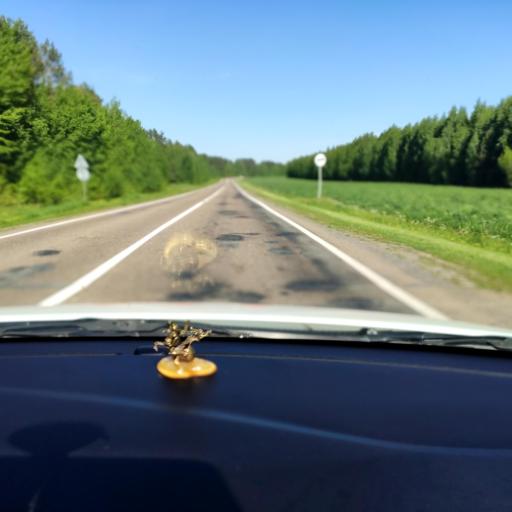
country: RU
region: Tatarstan
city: Vysokaya Gora
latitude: 56.0679
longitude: 49.1982
